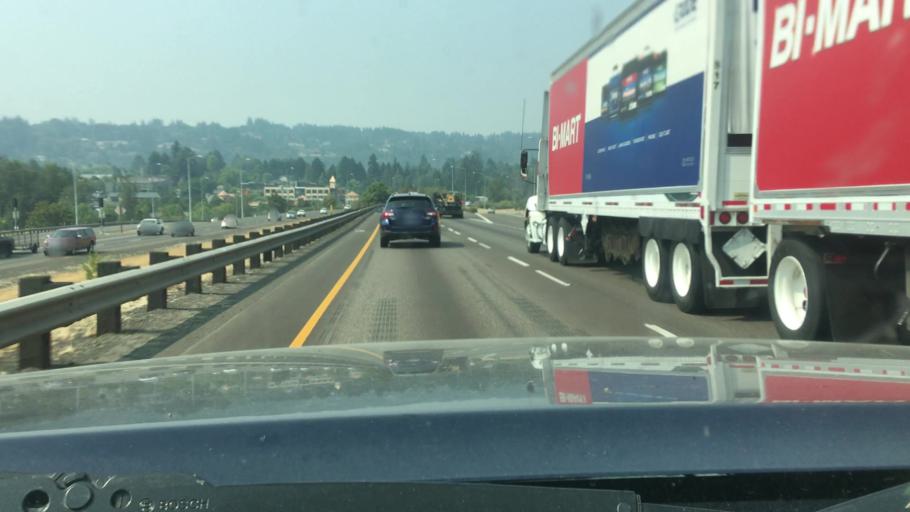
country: US
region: Oregon
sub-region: Clackamas County
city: West Linn
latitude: 45.3484
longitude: -122.6453
